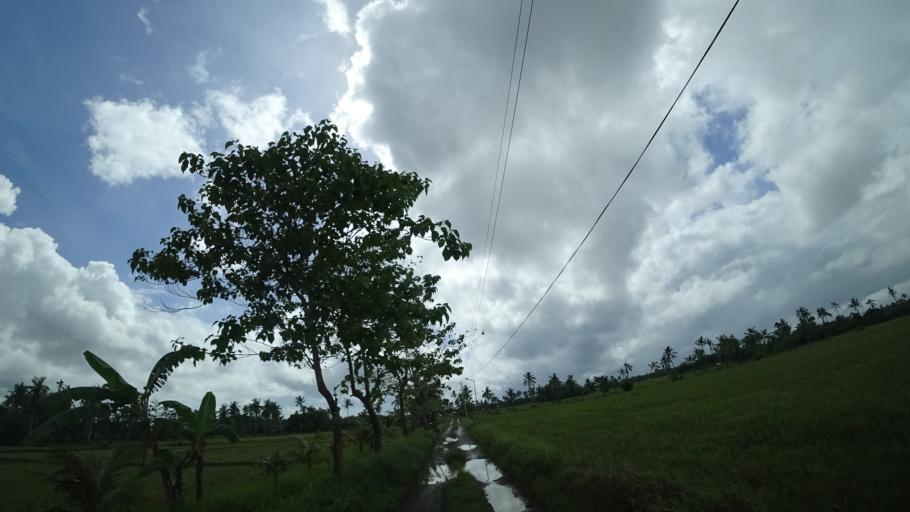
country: PH
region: Eastern Visayas
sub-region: Province of Leyte
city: Cabacungan
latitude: 10.9161
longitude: 124.9812
